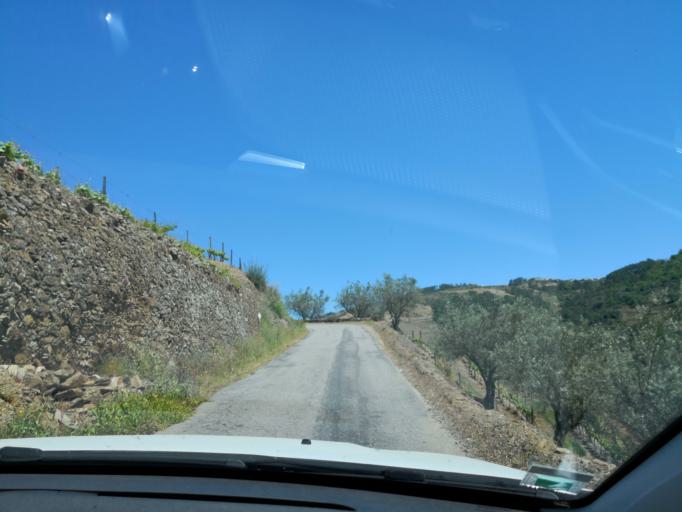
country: PT
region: Vila Real
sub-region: Vila Real
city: Vila Real
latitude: 41.2318
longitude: -7.7199
